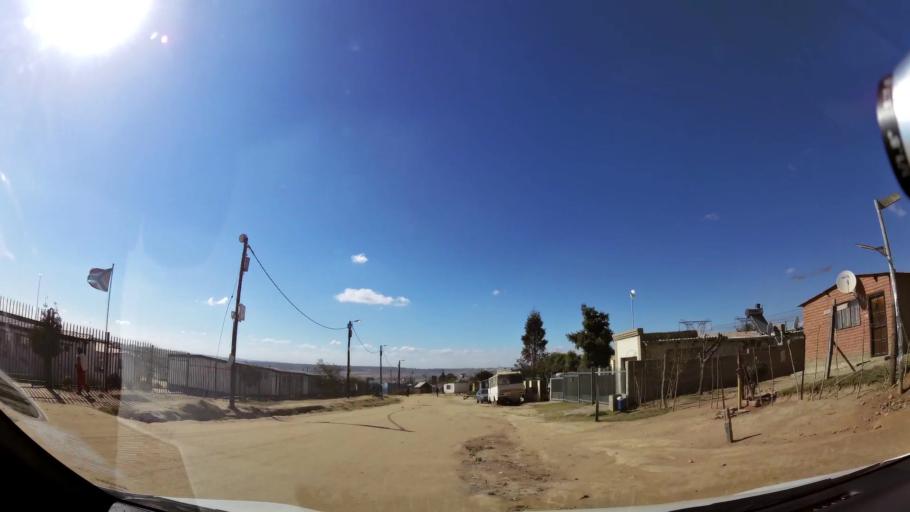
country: ZA
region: Gauteng
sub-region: City of Johannesburg Metropolitan Municipality
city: Diepsloot
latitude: -25.9202
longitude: 28.0863
